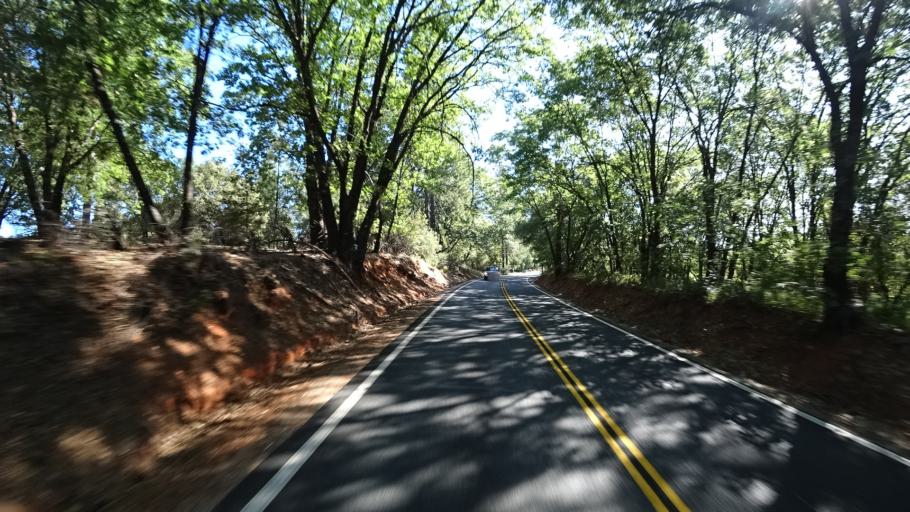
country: US
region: California
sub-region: Amador County
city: Pioneer
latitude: 38.4120
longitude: -120.5523
